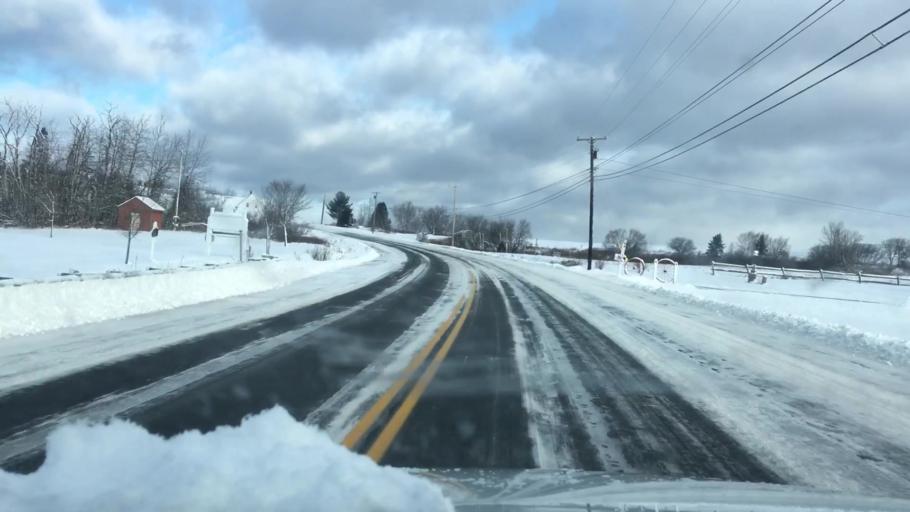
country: US
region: Maine
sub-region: Aroostook County
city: Caribou
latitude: 46.9474
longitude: -68.0224
